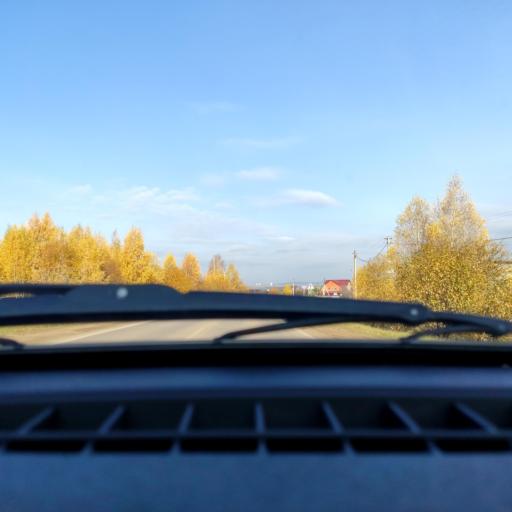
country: RU
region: Bashkortostan
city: Kabakovo
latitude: 54.7078
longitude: 56.1684
